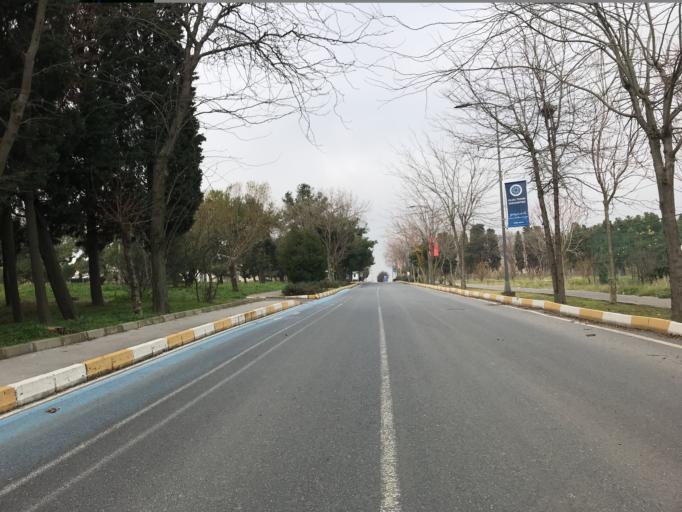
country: TR
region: Istanbul
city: merter keresteciler
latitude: 41.0226
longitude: 28.8908
